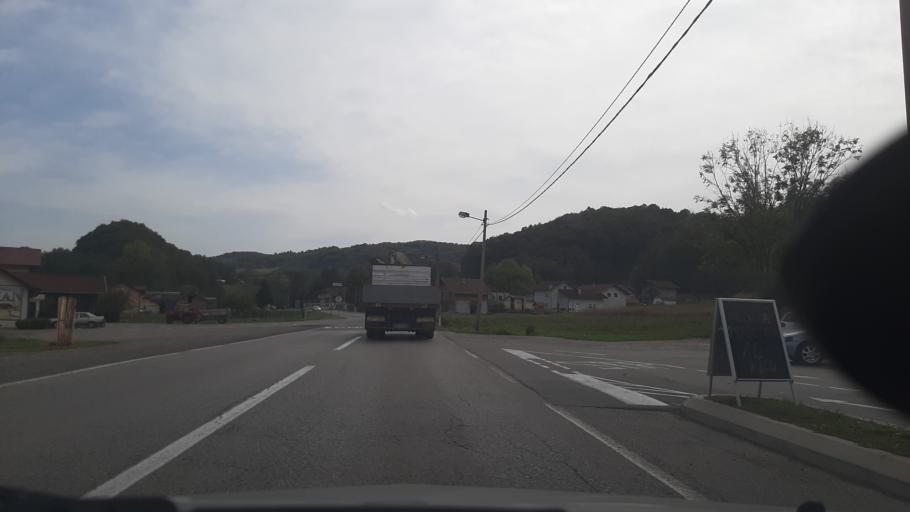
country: BA
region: Republika Srpska
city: Maglajani
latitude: 44.8564
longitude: 17.4402
